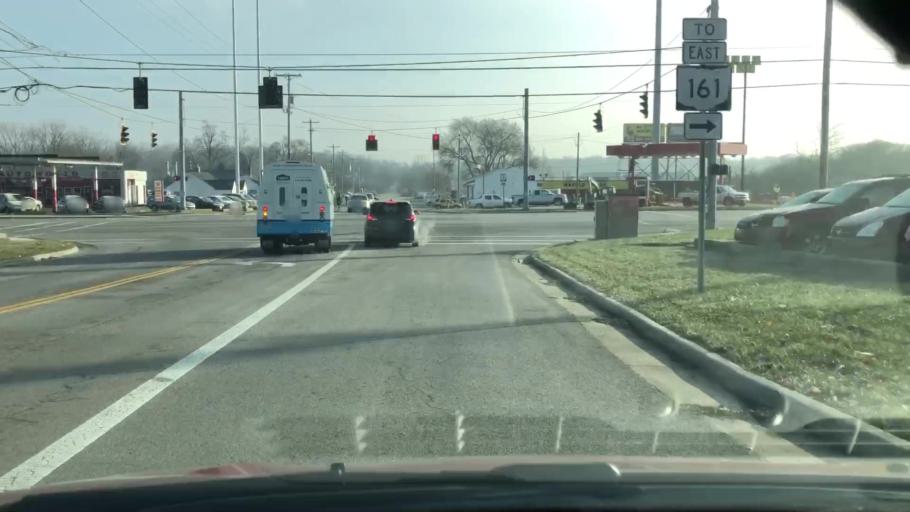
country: US
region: Ohio
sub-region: Franklin County
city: Huber Ridge
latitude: 40.0807
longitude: -82.9291
